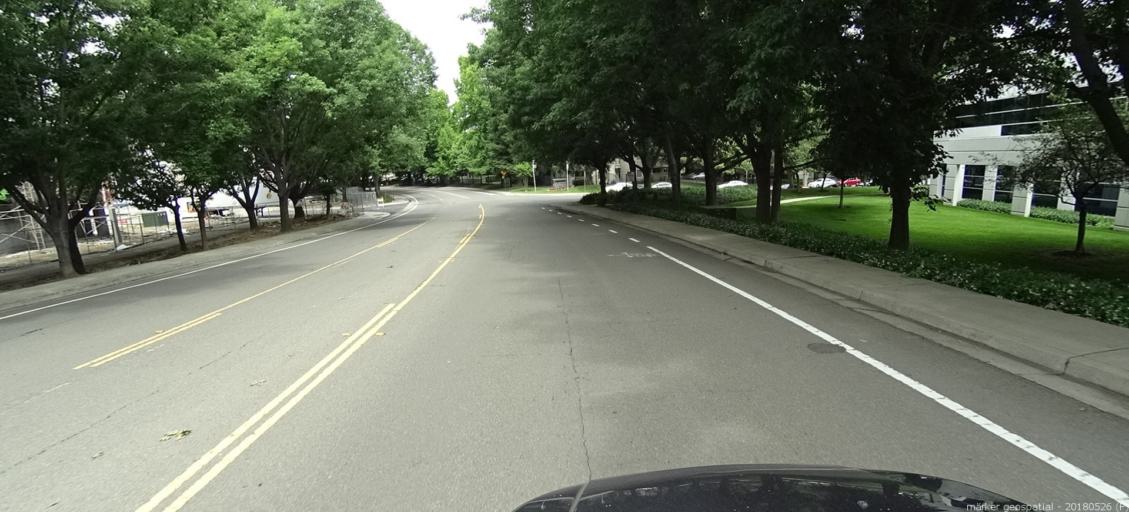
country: US
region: California
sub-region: Sacramento County
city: Sacramento
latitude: 38.6087
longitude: -121.5026
